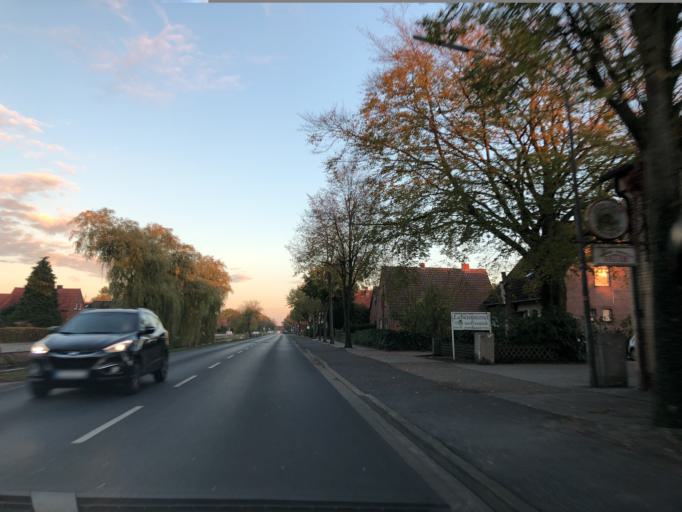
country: DE
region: Lower Saxony
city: Papenburg
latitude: 53.0818
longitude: 7.4149
